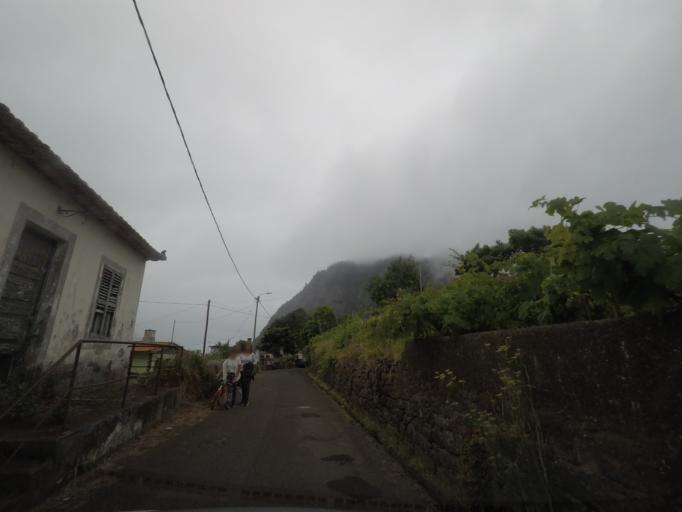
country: PT
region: Madeira
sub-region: Santana
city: Santana
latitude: 32.7683
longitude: -16.8433
